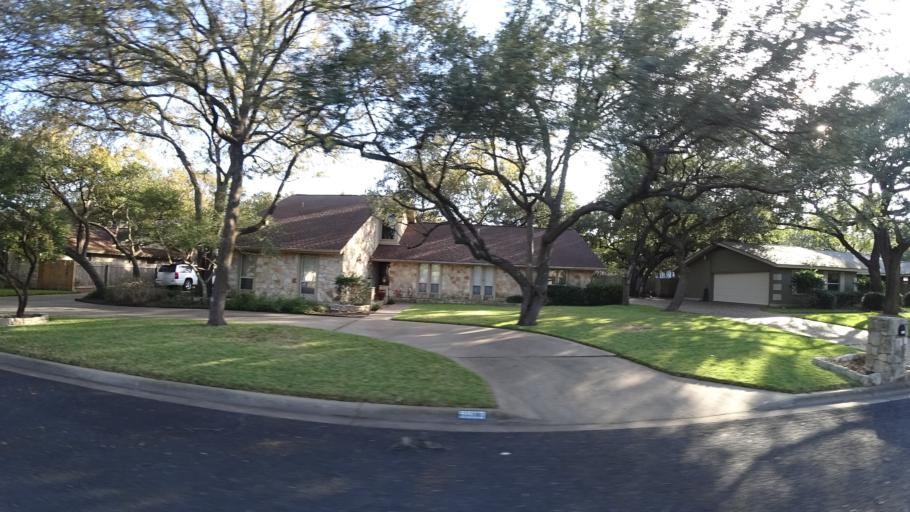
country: US
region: Texas
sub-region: Williamson County
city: Anderson Mill
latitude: 30.4359
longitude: -97.8044
